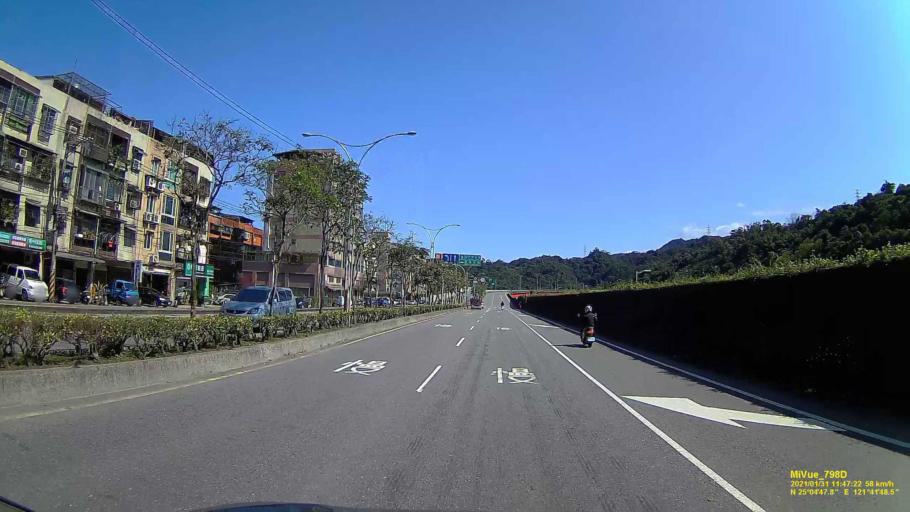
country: TW
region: Taiwan
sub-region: Keelung
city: Keelung
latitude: 25.0790
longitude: 121.6969
